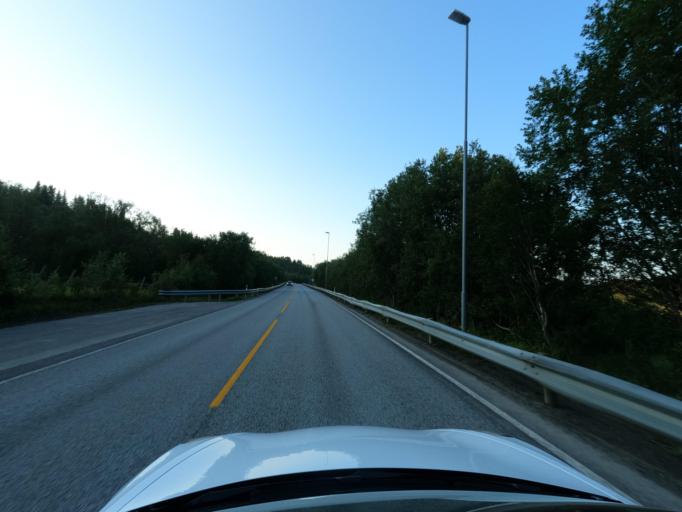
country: NO
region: Troms
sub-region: Harstad
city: Harstad
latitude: 68.7344
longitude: 16.5531
